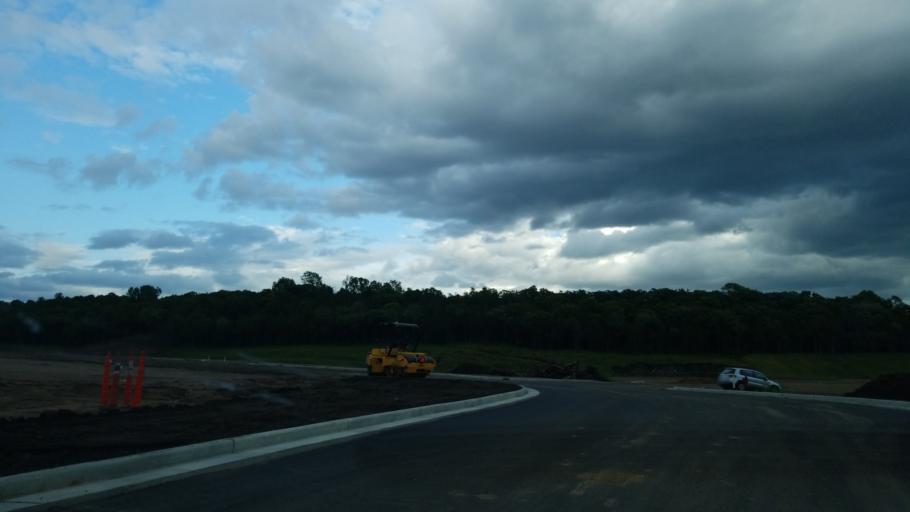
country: US
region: Minnesota
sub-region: Washington County
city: Lakeland
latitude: 44.9451
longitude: -92.7266
